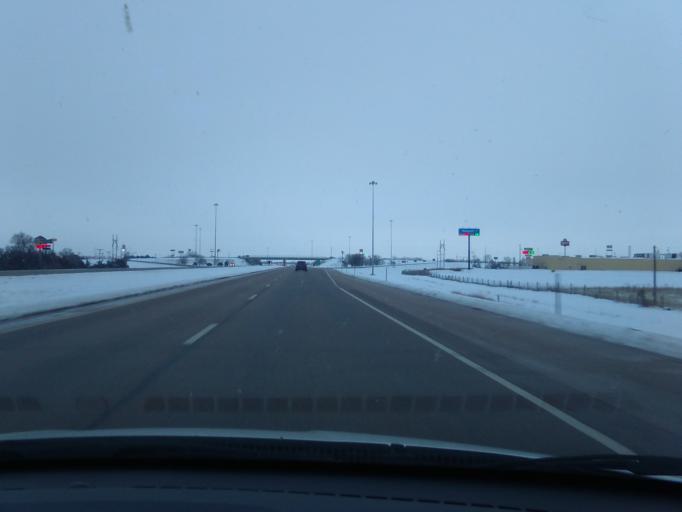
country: US
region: Nebraska
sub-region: Keith County
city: Ogallala
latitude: 41.1151
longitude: -101.7228
